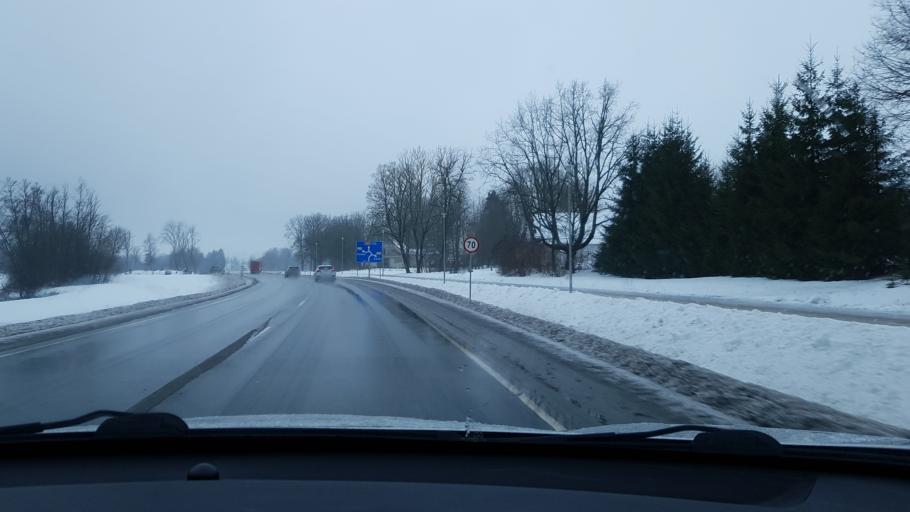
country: EE
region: Jaervamaa
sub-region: Tueri vald
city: Tueri
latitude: 58.8518
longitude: 25.4812
